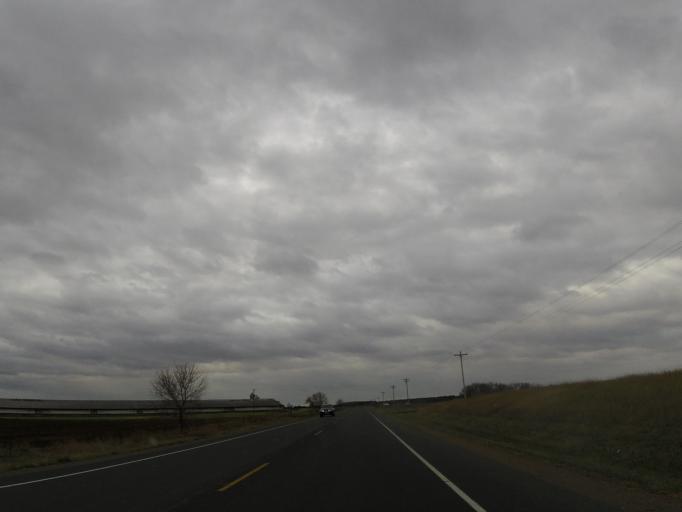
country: US
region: Wisconsin
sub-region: Saint Croix County
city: New Richmond
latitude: 45.0976
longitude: -92.5616
